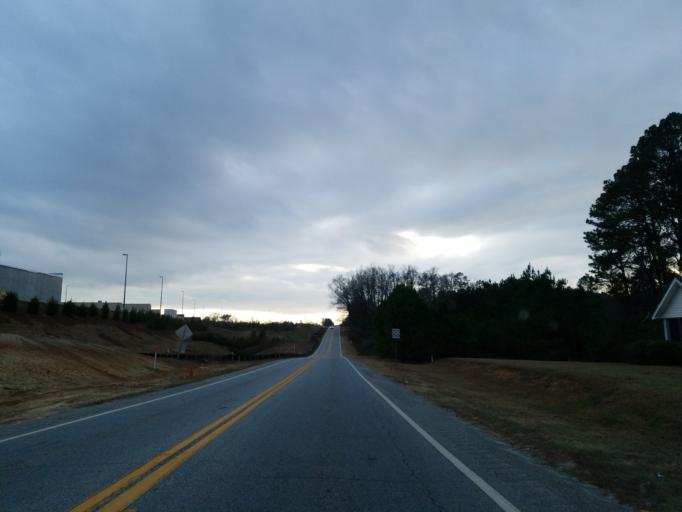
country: US
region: Georgia
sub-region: Dawson County
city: Dawsonville
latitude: 34.3539
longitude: -84.0521
